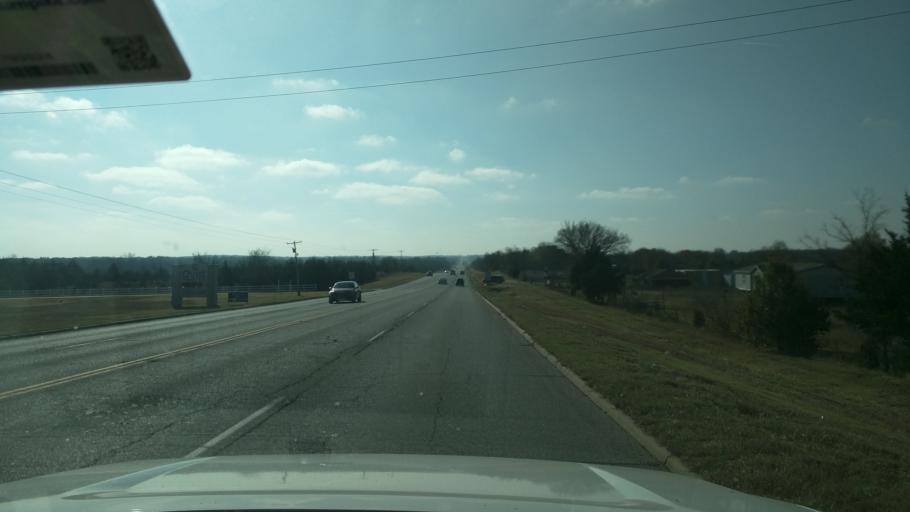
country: US
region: Oklahoma
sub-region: Washington County
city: Bartlesville
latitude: 36.6824
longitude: -95.9352
